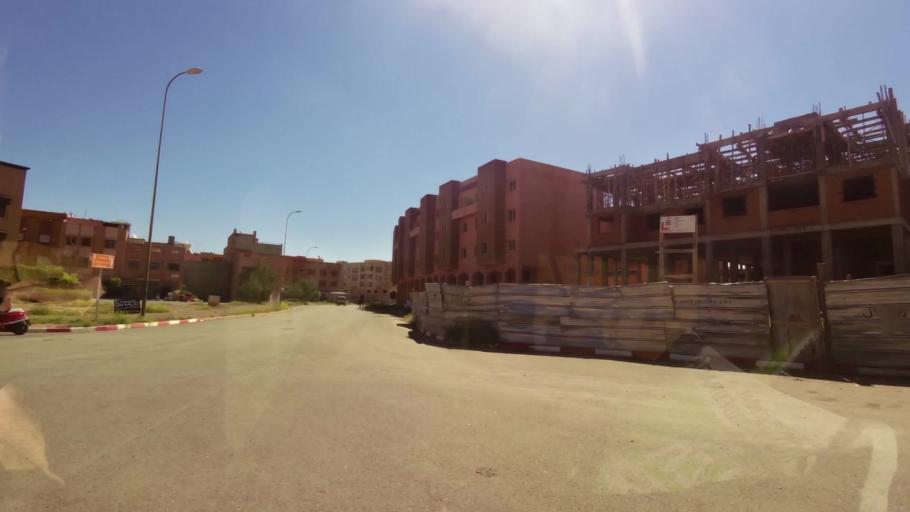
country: MA
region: Marrakech-Tensift-Al Haouz
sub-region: Marrakech
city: Marrakesh
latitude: 31.5773
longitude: -8.0575
